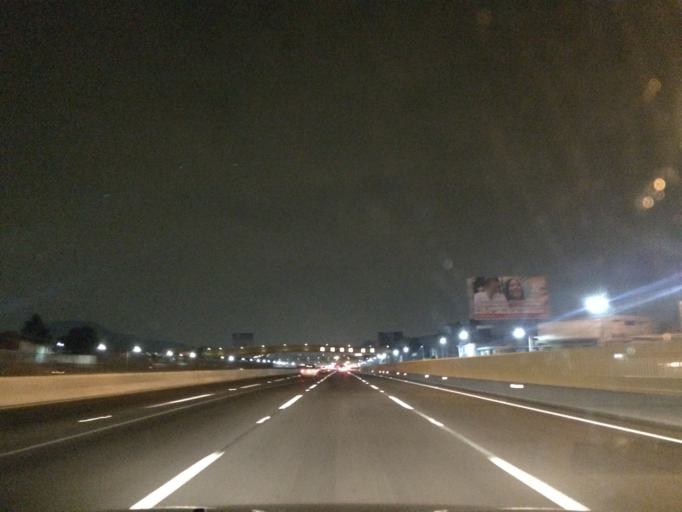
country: MX
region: Mexico
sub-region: La Paz
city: San Isidro
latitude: 19.3070
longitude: -98.9384
